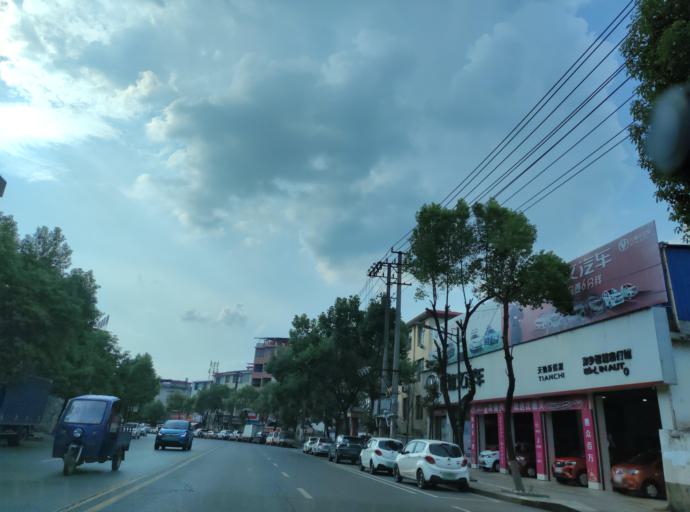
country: CN
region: Jiangxi Sheng
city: Pingxiang
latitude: 27.6610
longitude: 113.8382
